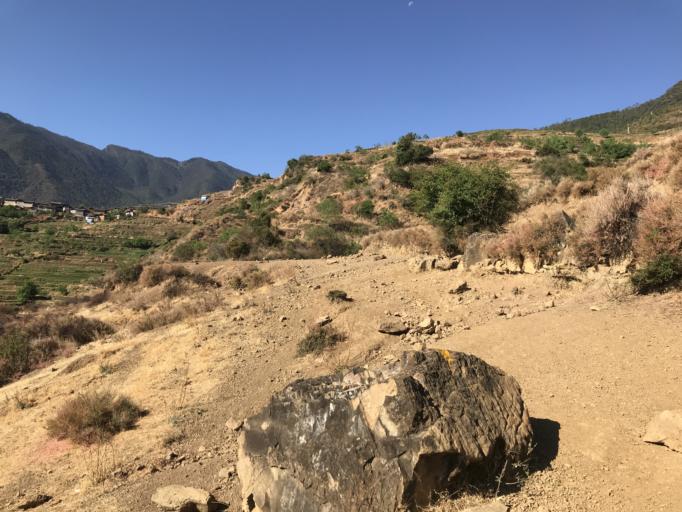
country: CN
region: Yunnan
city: Shuijia
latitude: 27.4099
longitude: 100.4523
